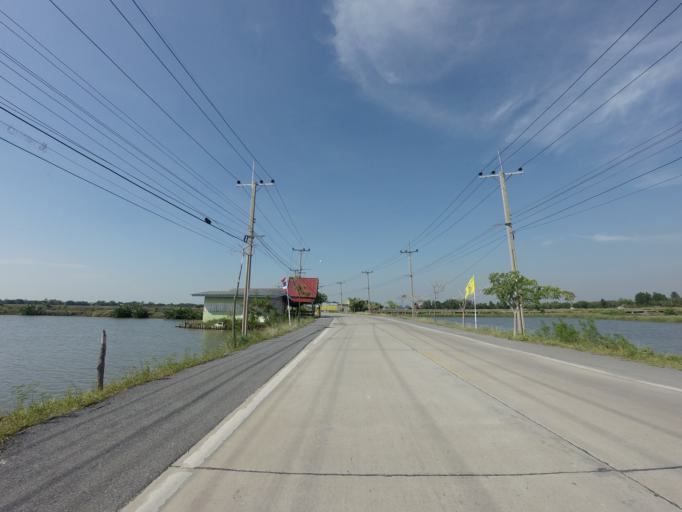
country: TH
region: Samut Prakan
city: Phra Samut Chedi
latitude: 13.5492
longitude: 100.5278
